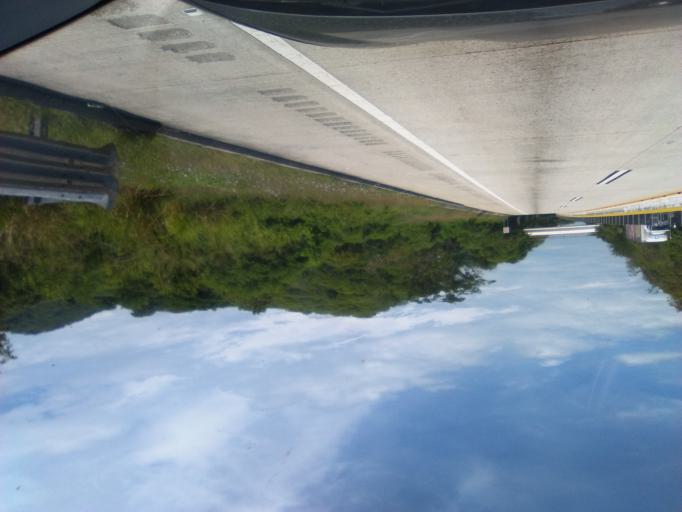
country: MX
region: Guerrero
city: Xaltianguis
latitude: 17.0089
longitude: -99.6643
